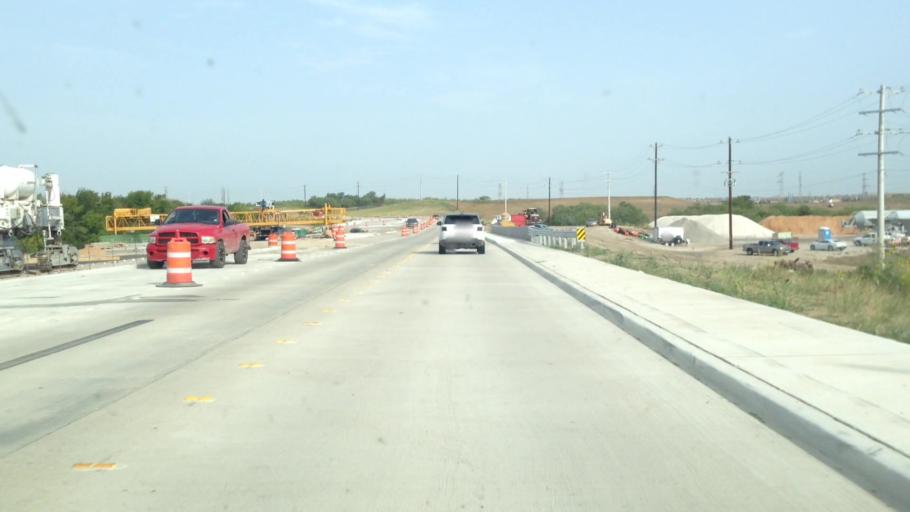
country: US
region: Texas
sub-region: Denton County
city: The Colony
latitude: 33.0458
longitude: -96.8921
